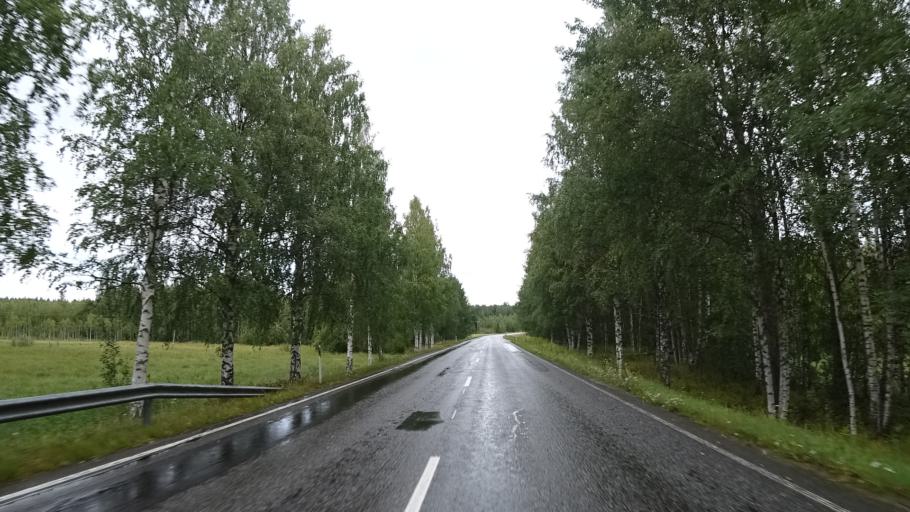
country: FI
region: Southern Savonia
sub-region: Savonlinna
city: Kerimaeki
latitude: 62.0338
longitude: 29.5185
